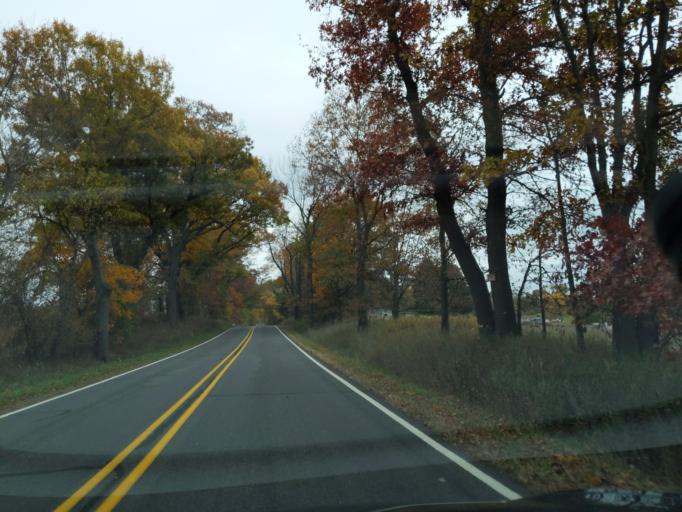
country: US
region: Michigan
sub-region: Eaton County
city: Eaton Rapids
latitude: 42.3856
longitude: -84.6005
